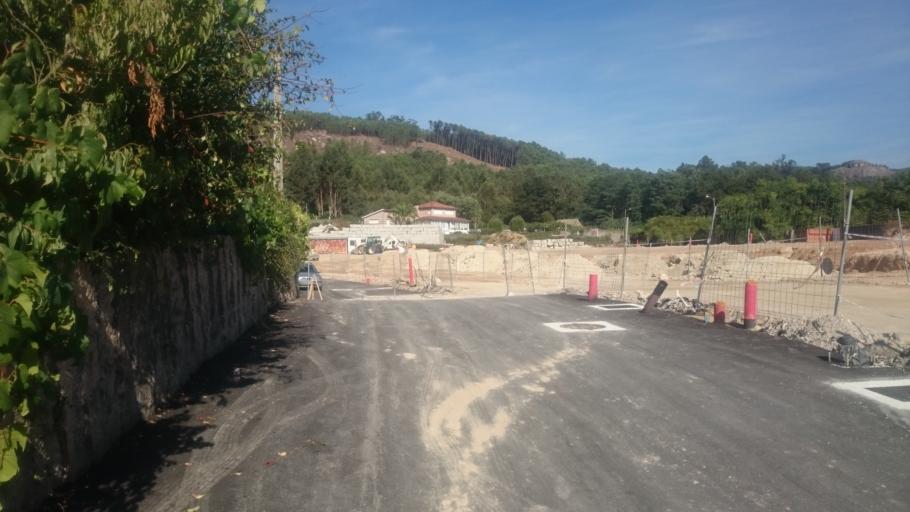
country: ES
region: Galicia
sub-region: Provincia de Pontevedra
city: Porrino
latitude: 42.1632
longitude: -8.6156
